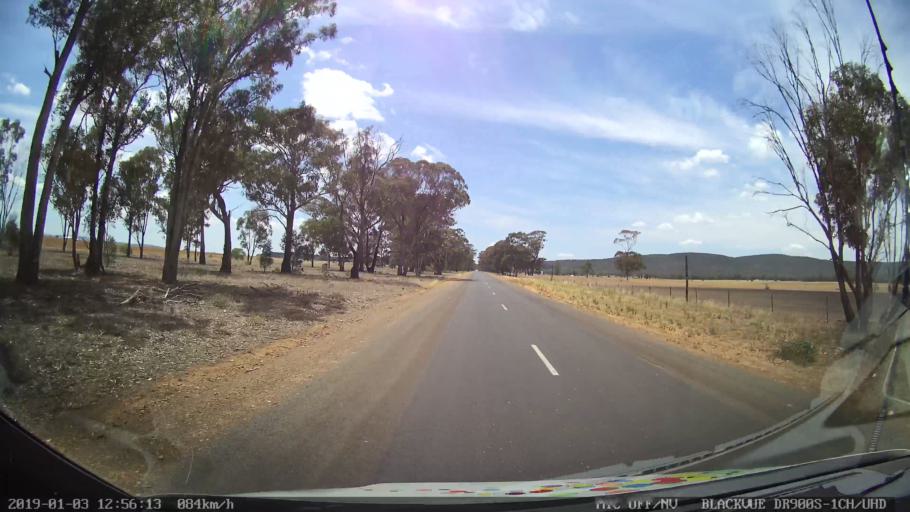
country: AU
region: New South Wales
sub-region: Weddin
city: Grenfell
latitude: -33.6462
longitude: 148.3420
